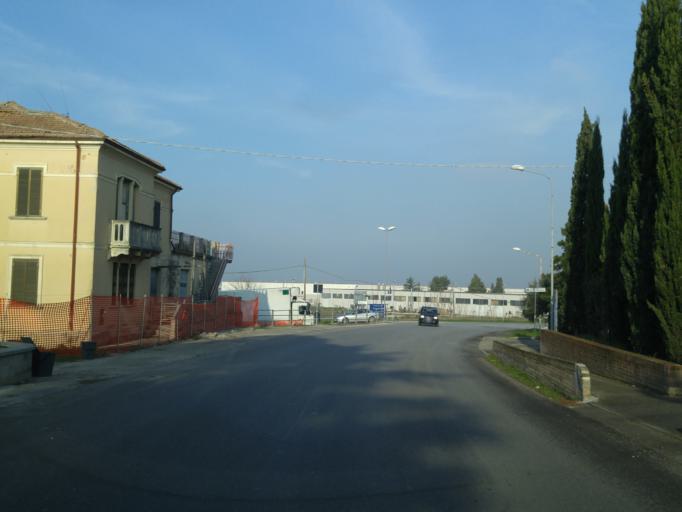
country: IT
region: The Marches
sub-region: Provincia di Pesaro e Urbino
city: Villanova
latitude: 43.7301
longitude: 12.9220
